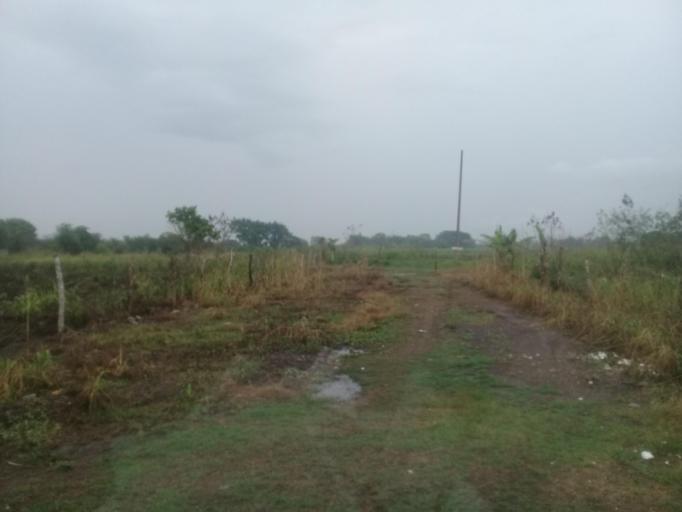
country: MX
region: Veracruz
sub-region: La Antigua
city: Nicolas Blanco (San Pancho)
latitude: 19.3573
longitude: -96.3540
